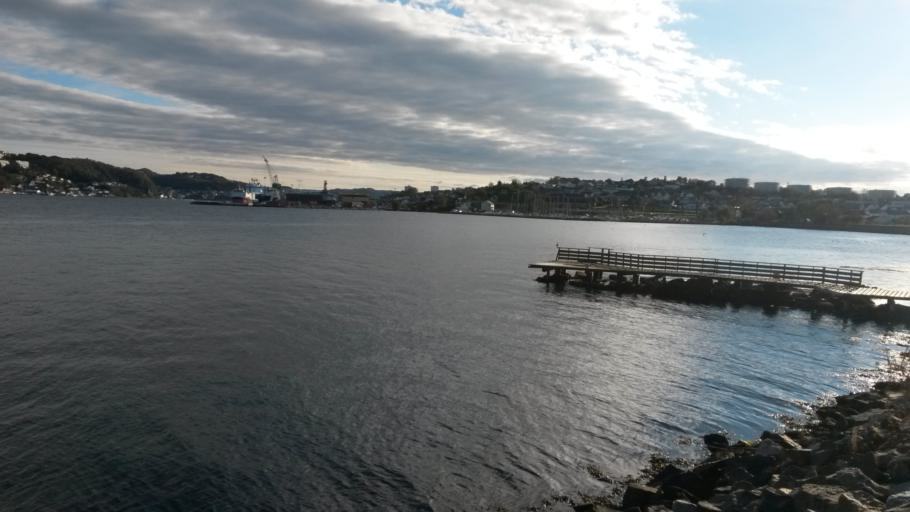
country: NO
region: Rogaland
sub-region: Sandnes
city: Sandnes
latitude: 58.8767
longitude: 5.7449
